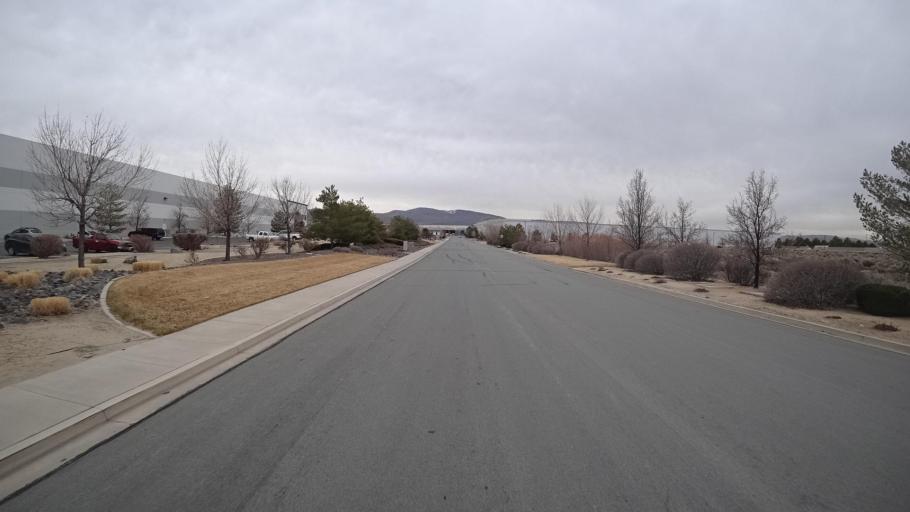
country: US
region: Nevada
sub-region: Washoe County
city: Spanish Springs
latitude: 39.6766
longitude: -119.7140
